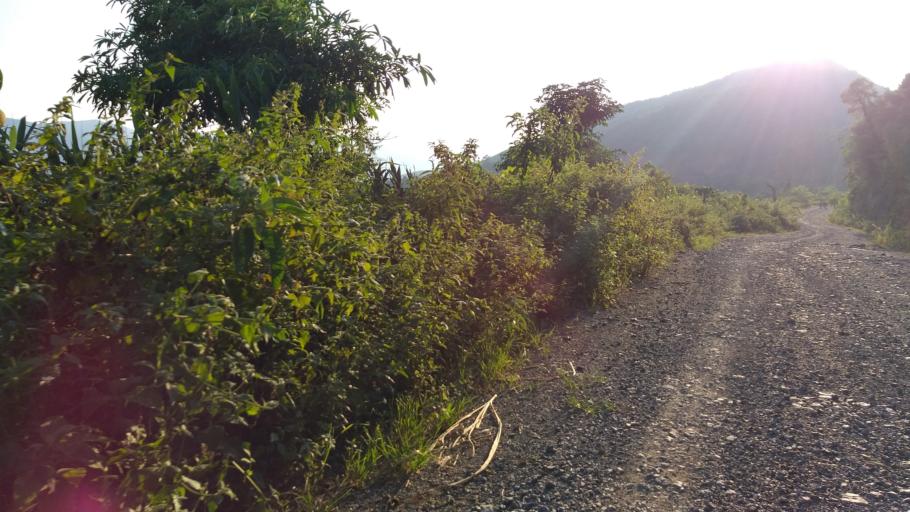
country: LA
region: Phongsali
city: Khoa
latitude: 21.1985
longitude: 102.5736
